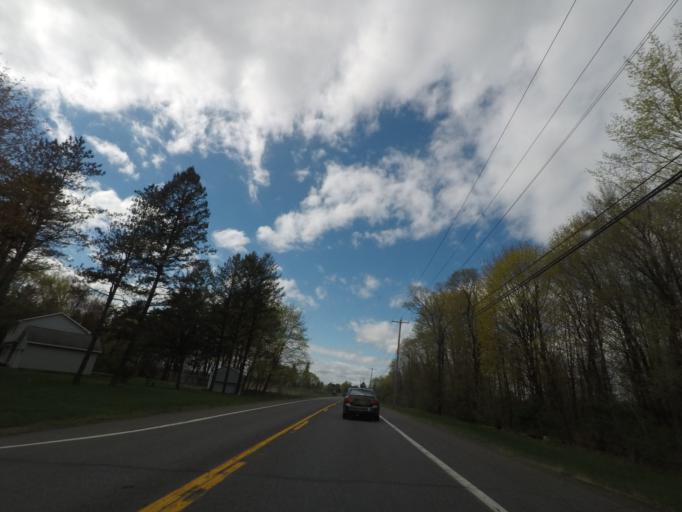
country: US
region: New York
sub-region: Columbia County
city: Niverville
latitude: 42.4469
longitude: -73.6878
